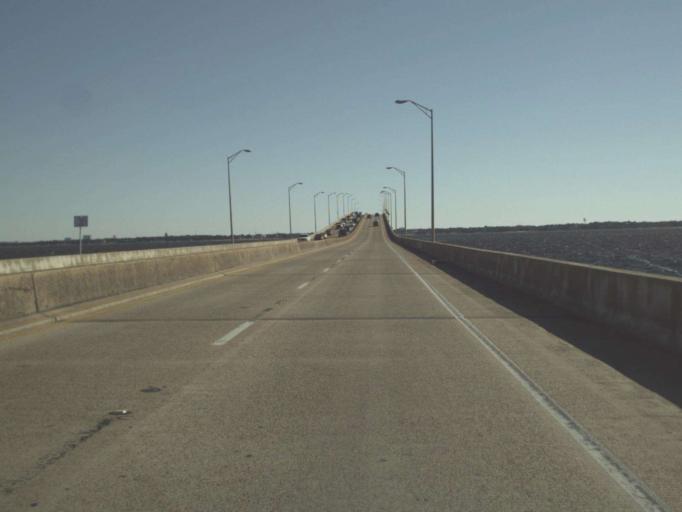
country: US
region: Florida
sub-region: Escambia County
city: East Pensacola Heights
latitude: 30.3999
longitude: -87.1871
